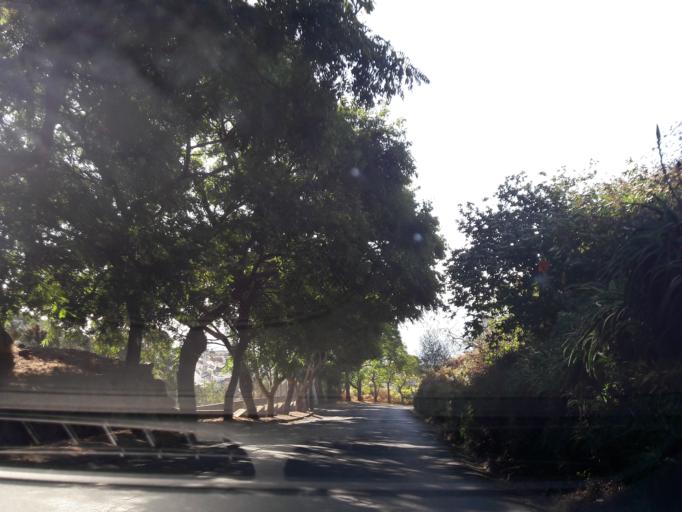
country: PT
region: Madeira
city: Canico
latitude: 32.6506
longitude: -16.8617
